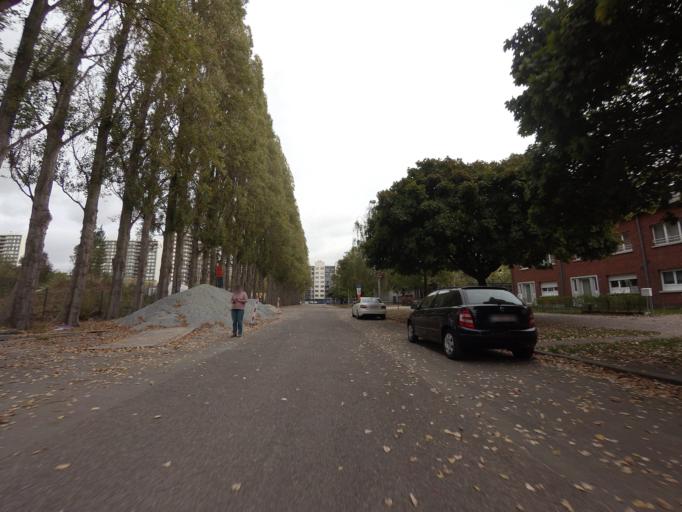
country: BE
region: Flanders
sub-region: Provincie Antwerpen
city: Antwerpen
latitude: 51.2235
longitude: 4.3759
